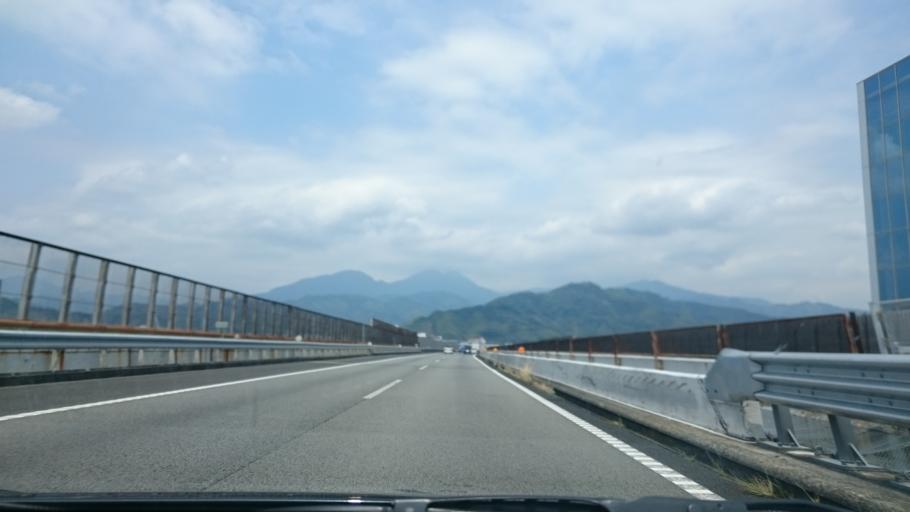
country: JP
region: Shizuoka
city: Shizuoka-shi
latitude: 34.9968
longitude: 138.4341
